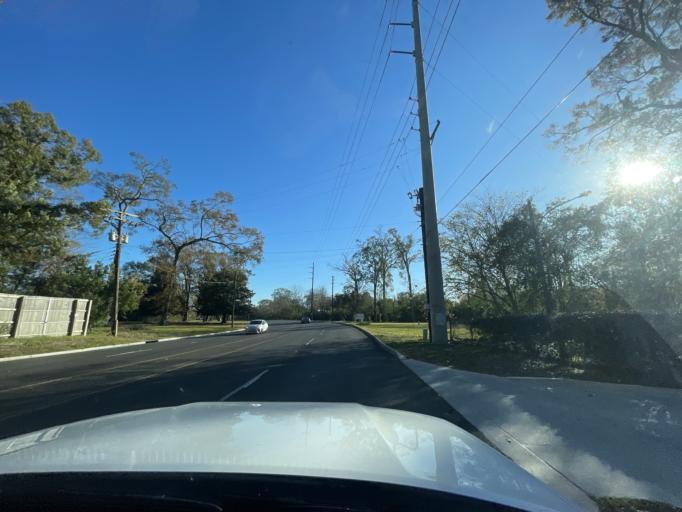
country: US
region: Louisiana
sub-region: East Baton Rouge Parish
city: Baton Rouge
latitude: 30.4293
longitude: -91.1528
